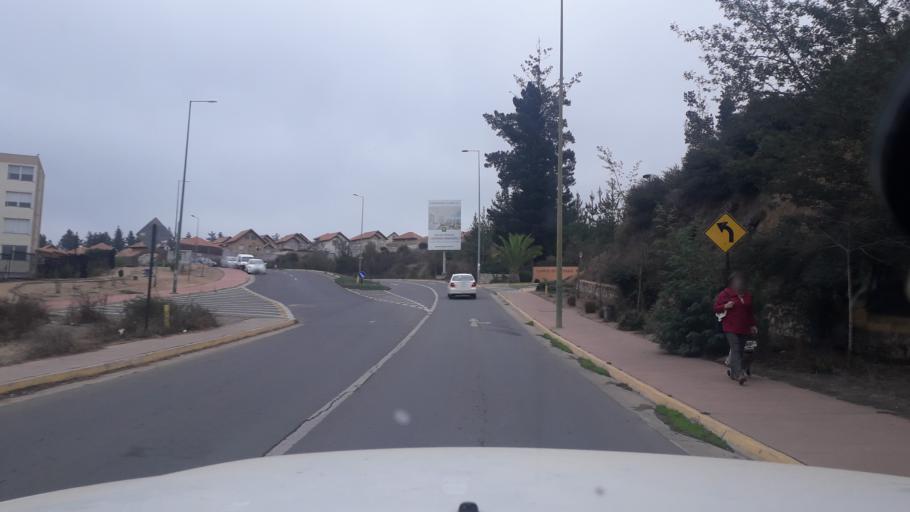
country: CL
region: Valparaiso
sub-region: Provincia de Valparaiso
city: Valparaiso
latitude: -33.1340
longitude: -71.5700
